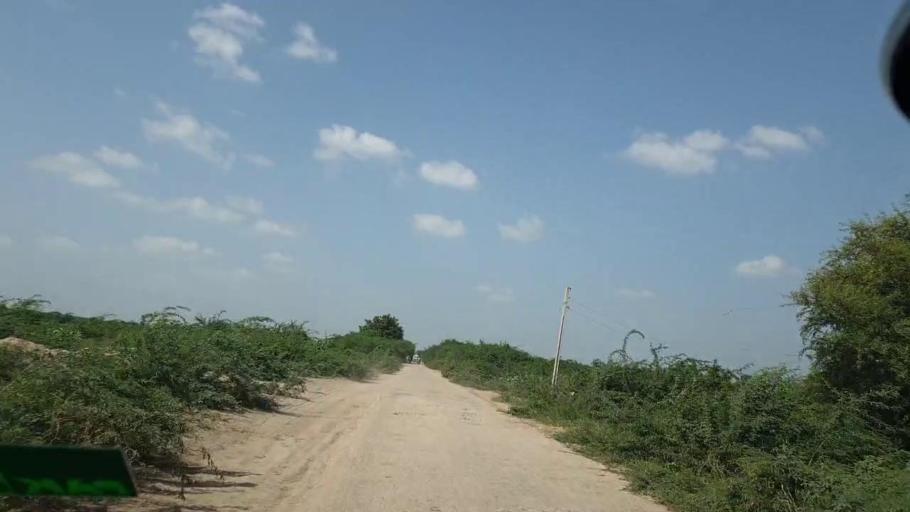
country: PK
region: Sindh
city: Naukot
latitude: 24.6383
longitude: 69.2273
